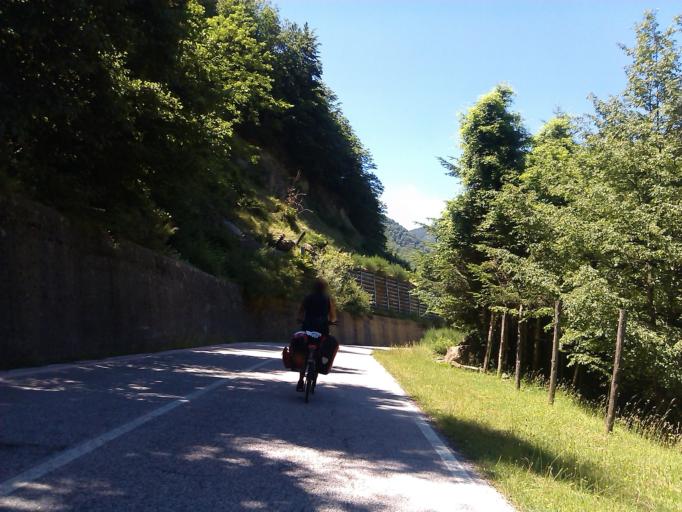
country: IT
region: Tuscany
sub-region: Provincia di Prato
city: Cantagallo
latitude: 44.0470
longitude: 11.0422
